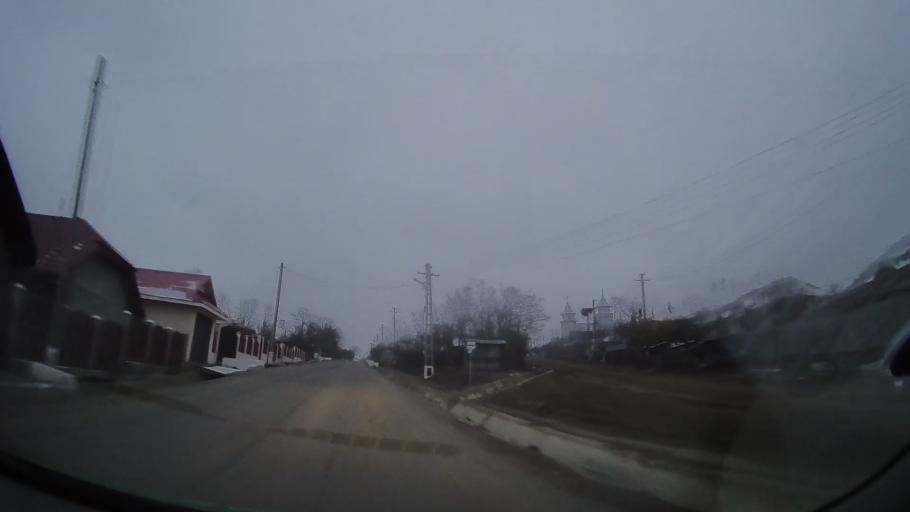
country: RO
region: Vaslui
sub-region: Comuna Gagesti
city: Gagesti
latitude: 46.3889
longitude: 27.9821
